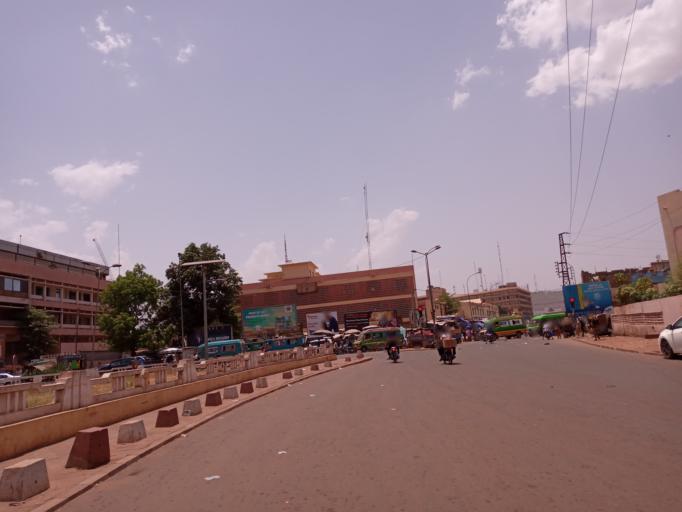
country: ML
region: Bamako
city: Bamako
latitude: 12.6388
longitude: -7.9964
